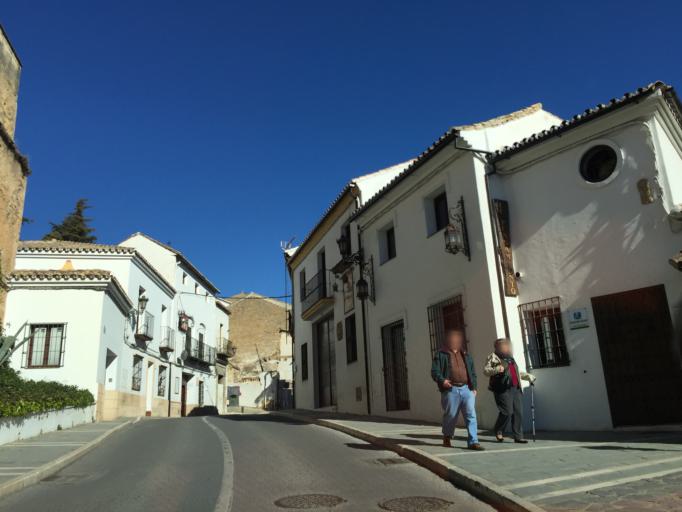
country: ES
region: Andalusia
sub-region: Provincia de Malaga
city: Ronda
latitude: 36.7363
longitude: -5.1643
